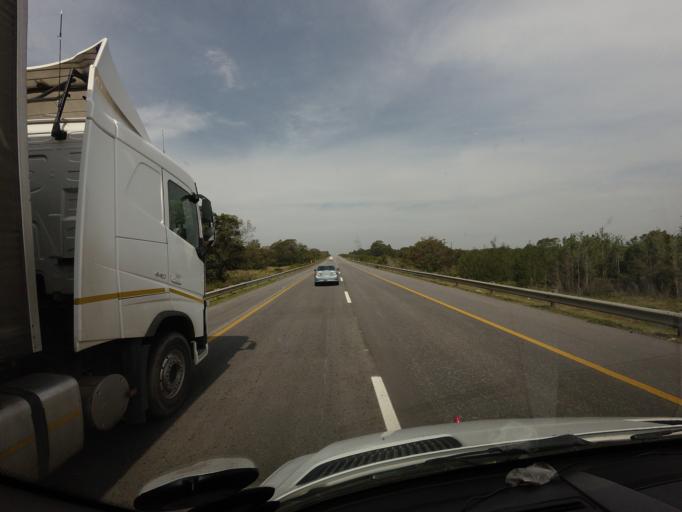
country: ZA
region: Eastern Cape
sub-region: Cacadu District Municipality
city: Kruisfontein
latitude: -33.9961
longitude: 24.7424
